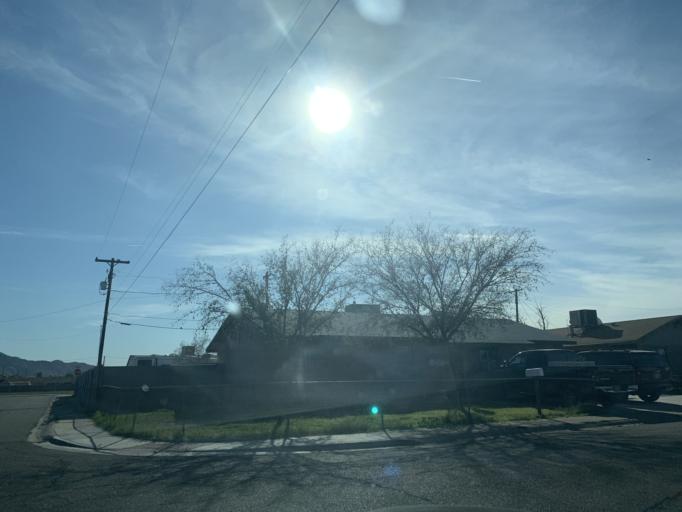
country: US
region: Arizona
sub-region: Maricopa County
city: Laveen
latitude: 33.4002
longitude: -112.1385
